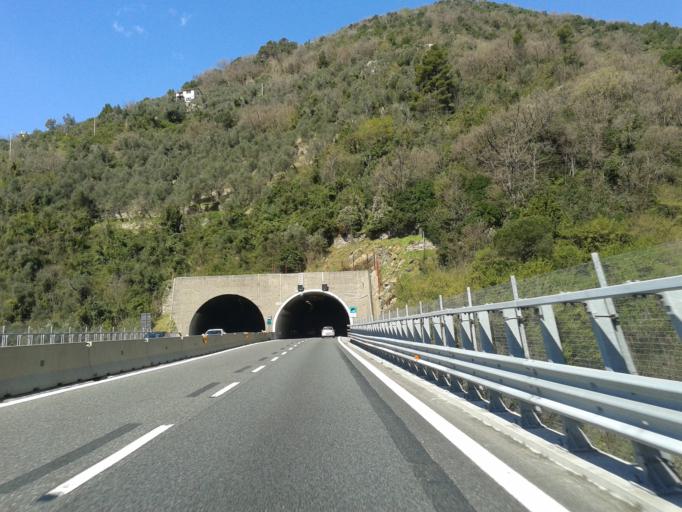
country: IT
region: Liguria
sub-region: Provincia di Genova
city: Zoagli
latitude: 44.3443
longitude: 9.2728
